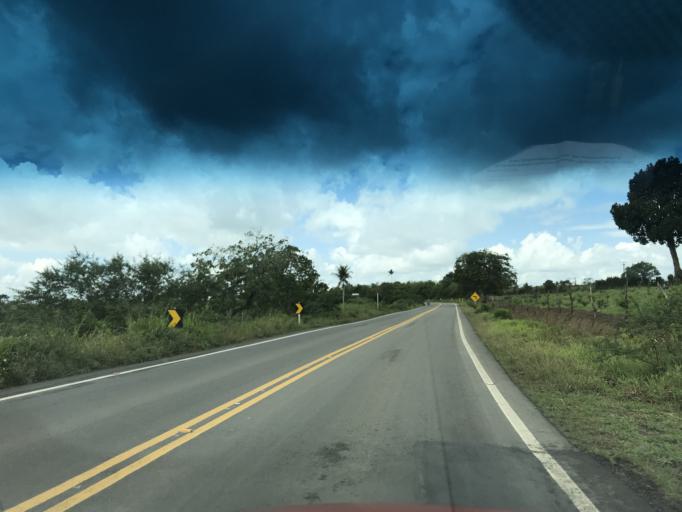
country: BR
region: Bahia
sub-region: Conceicao Do Almeida
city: Conceicao do Almeida
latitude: -12.7140
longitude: -39.2245
